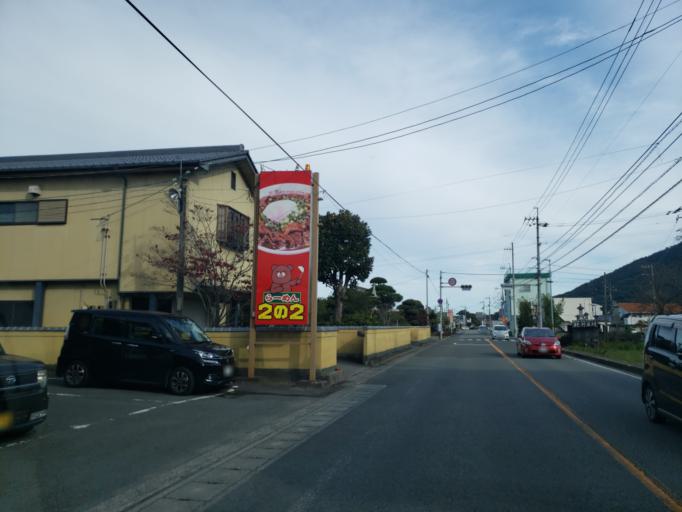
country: JP
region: Tokushima
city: Wakimachi
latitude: 34.0655
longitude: 134.1723
